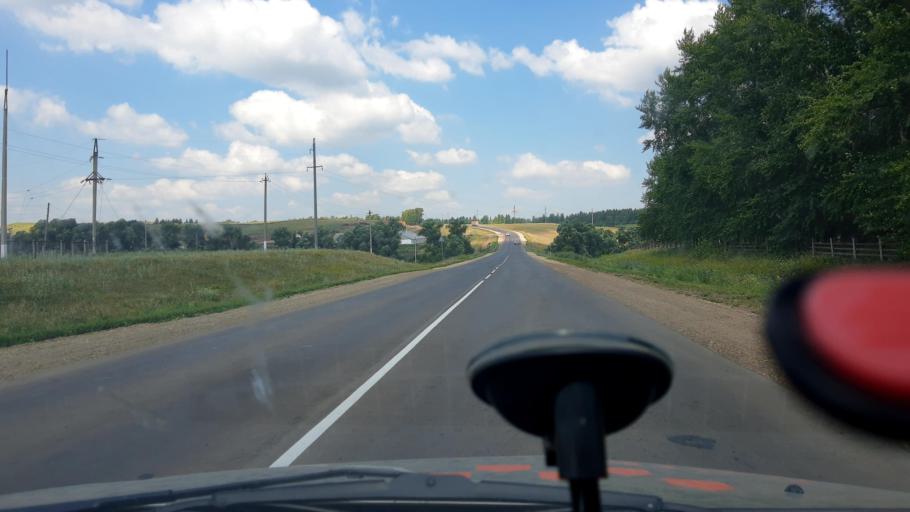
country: RU
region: Bashkortostan
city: Chekmagush
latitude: 54.9003
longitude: 54.5845
